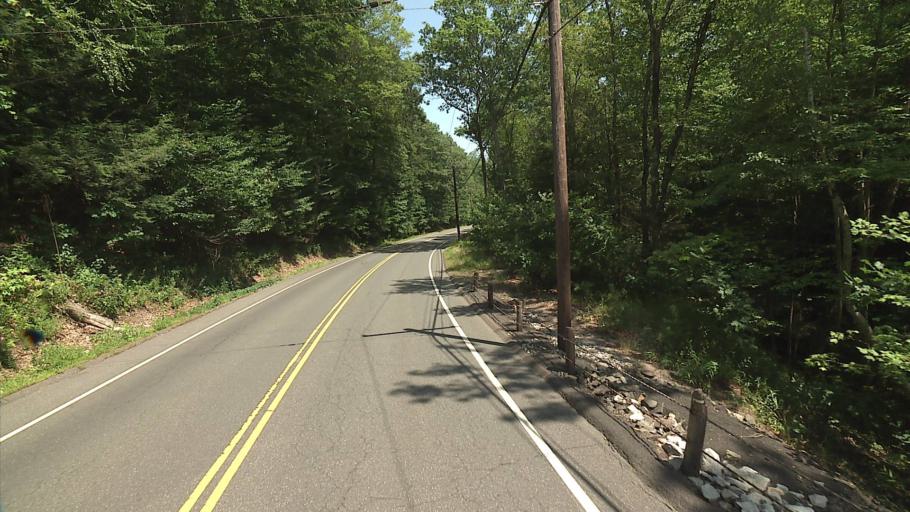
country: US
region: Connecticut
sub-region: Hartford County
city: North Granby
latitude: 41.9754
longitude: -72.8812
